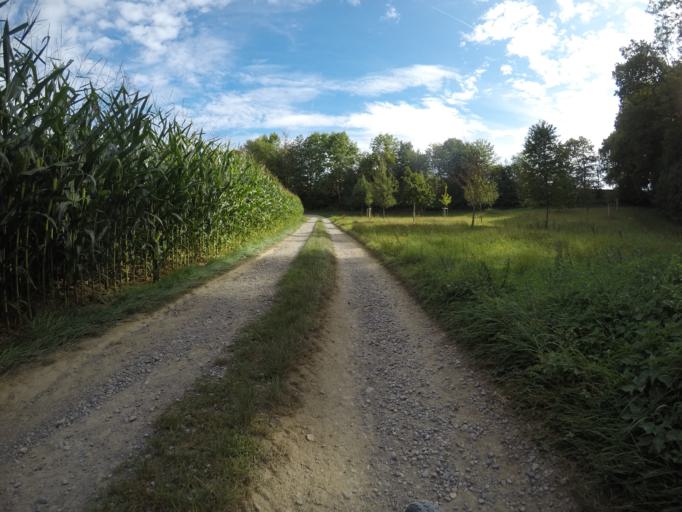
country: DE
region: Baden-Wuerttemberg
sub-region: Regierungsbezirk Stuttgart
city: Eberdingen
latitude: 48.8427
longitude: 8.9710
